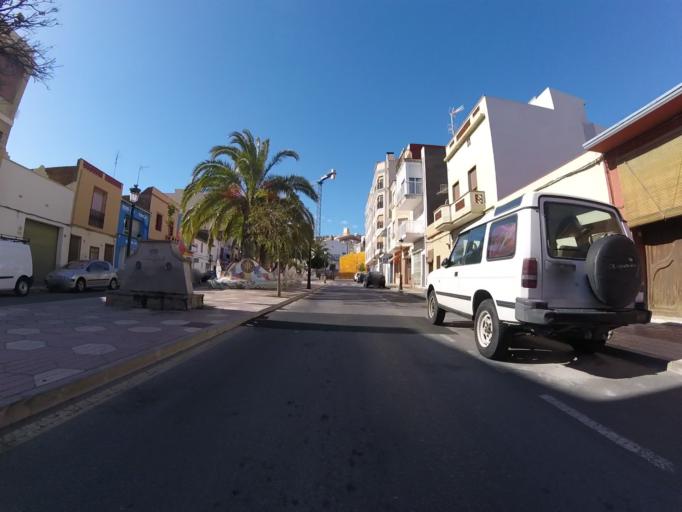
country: ES
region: Valencia
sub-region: Provincia de Castello
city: Orpesa/Oropesa del Mar
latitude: 40.0943
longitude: 0.1359
